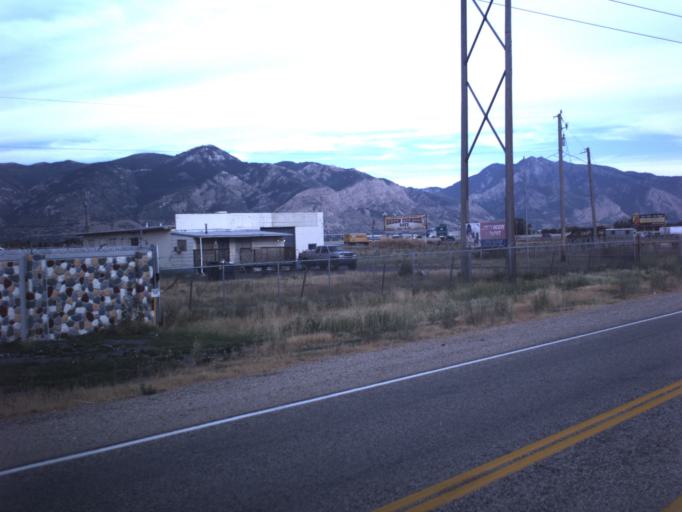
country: US
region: Utah
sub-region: Weber County
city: Farr West
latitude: 41.3201
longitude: -112.0295
